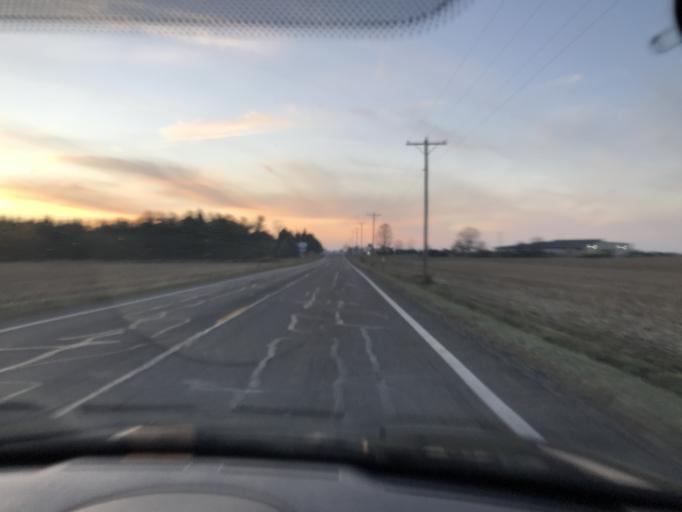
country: US
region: Ohio
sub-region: Champaign County
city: Urbana
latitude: 40.1075
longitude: -83.6871
